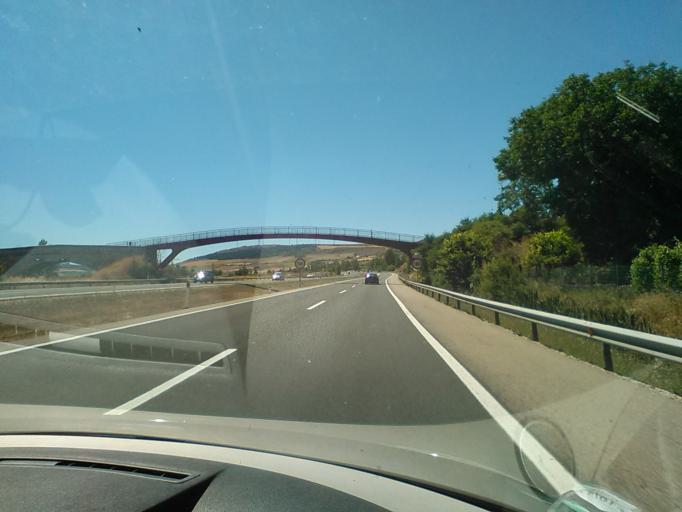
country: ES
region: Castille and Leon
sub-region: Provincia de Burgos
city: Quintanavides
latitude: 42.4802
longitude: -3.4234
